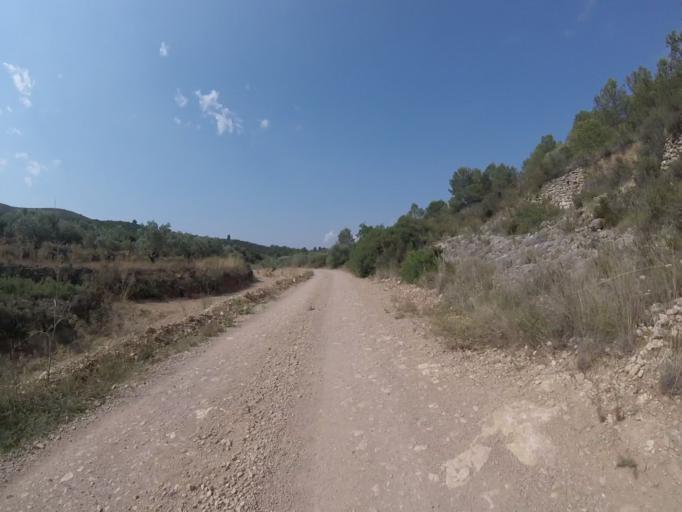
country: ES
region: Valencia
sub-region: Provincia de Castello
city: Cuevas de Vinroma
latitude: 40.3070
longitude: 0.1706
